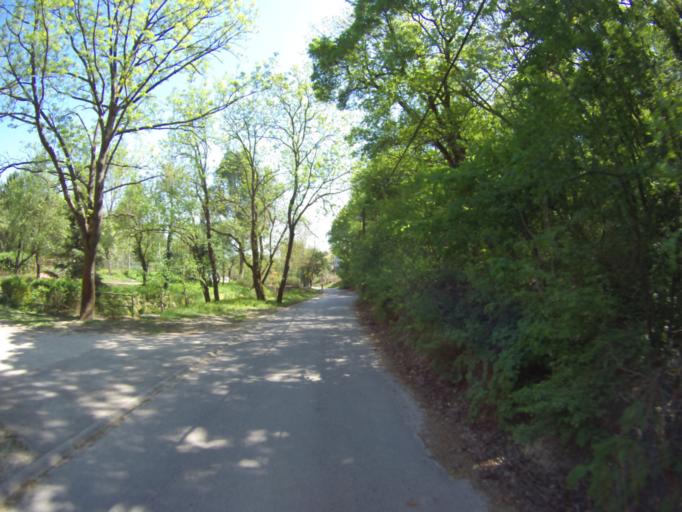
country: HU
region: Pest
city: Budaors
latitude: 47.4816
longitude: 18.9759
